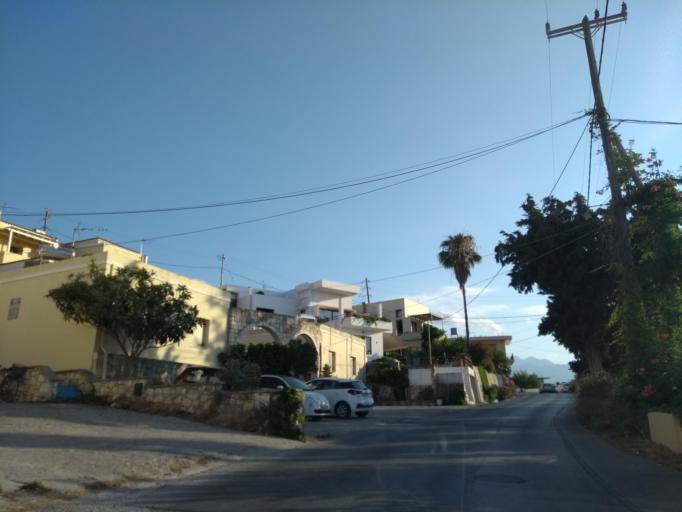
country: GR
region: Crete
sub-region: Nomos Chanias
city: Kalivai
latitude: 35.4498
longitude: 24.1755
